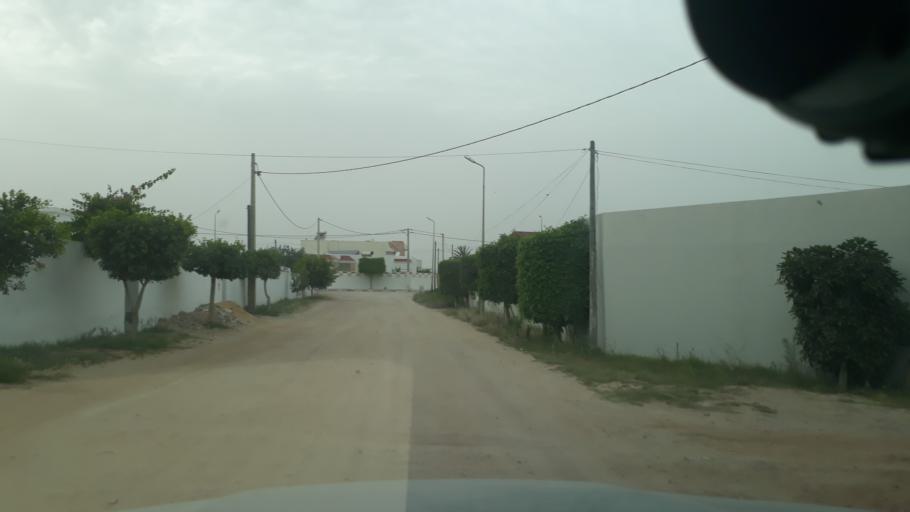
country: TN
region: Safaqis
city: Al Qarmadah
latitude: 34.7827
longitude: 10.7646
